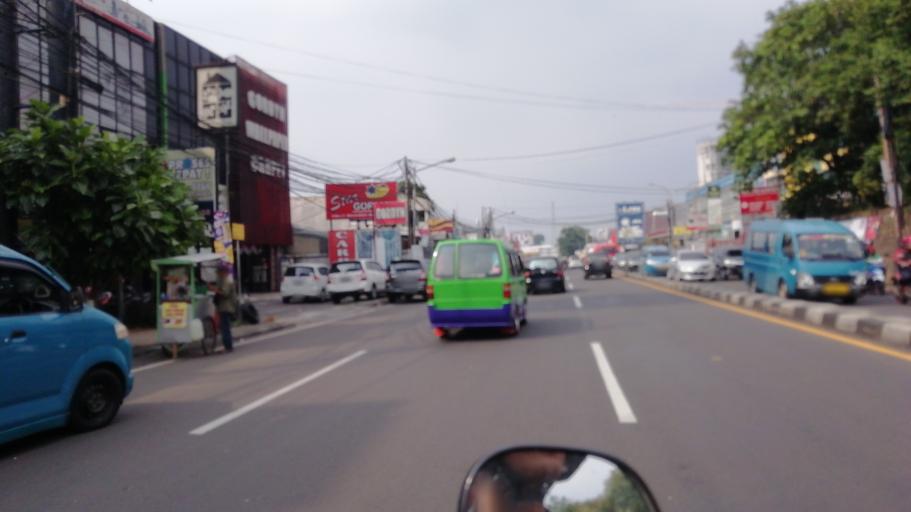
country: ID
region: West Java
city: Bogor
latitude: -6.5673
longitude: 106.8095
